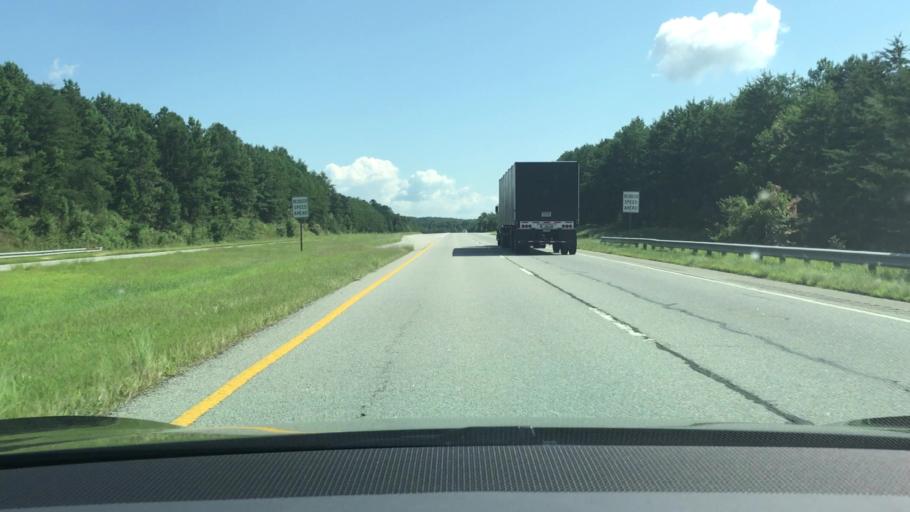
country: US
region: Georgia
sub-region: Habersham County
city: Clarkesville
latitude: 34.7057
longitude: -83.4089
